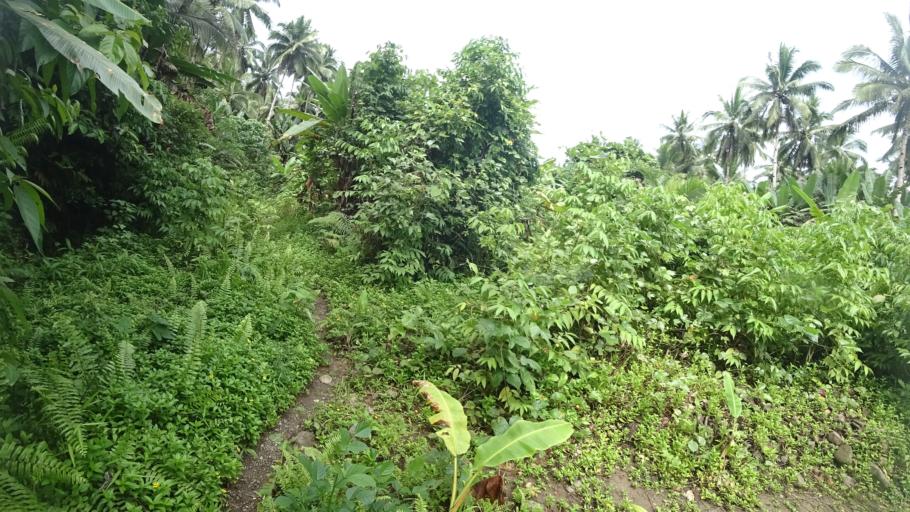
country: PH
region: Eastern Visayas
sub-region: Province of Leyte
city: Bugho
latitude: 10.8267
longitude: 124.8802
